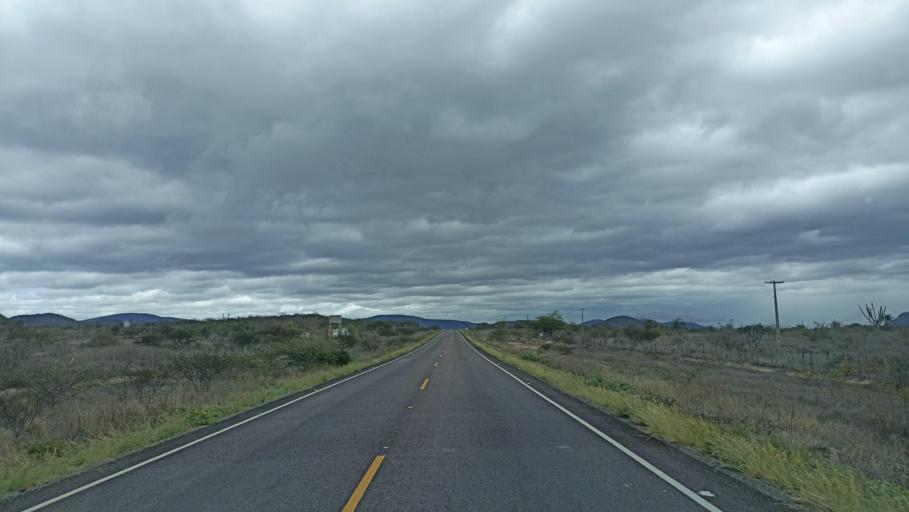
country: BR
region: Bahia
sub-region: Iacu
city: Iacu
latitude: -12.9080
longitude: -40.4067
